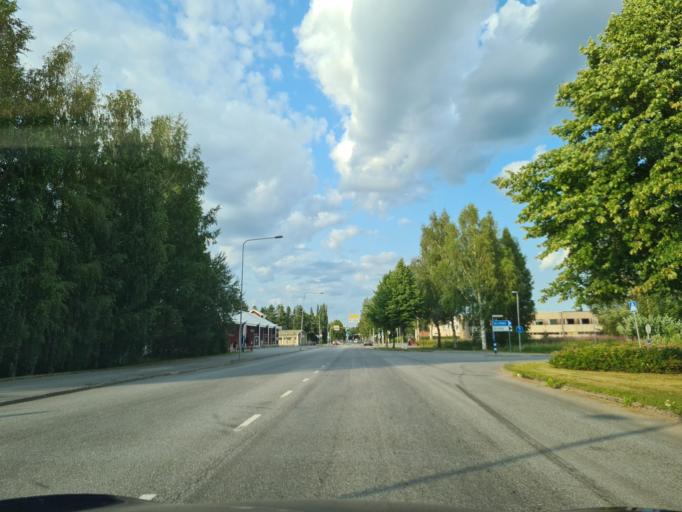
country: FI
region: Southern Ostrobothnia
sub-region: Seinaejoki
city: Lapua
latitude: 62.9695
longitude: 22.9944
